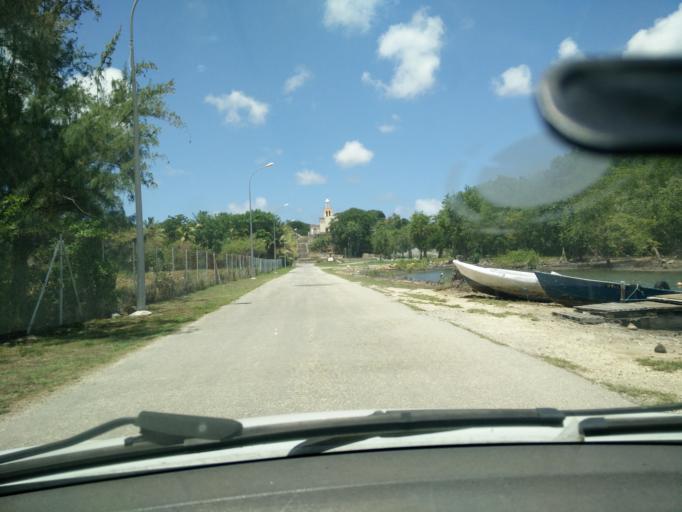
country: GP
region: Guadeloupe
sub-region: Guadeloupe
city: Petit-Canal
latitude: 16.3785
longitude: -61.4950
